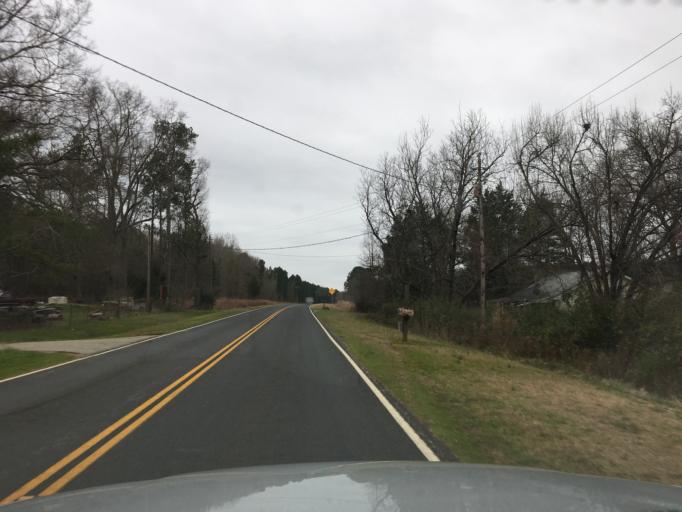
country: US
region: South Carolina
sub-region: Greenwood County
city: Greenwood
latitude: 34.1322
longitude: -82.1555
